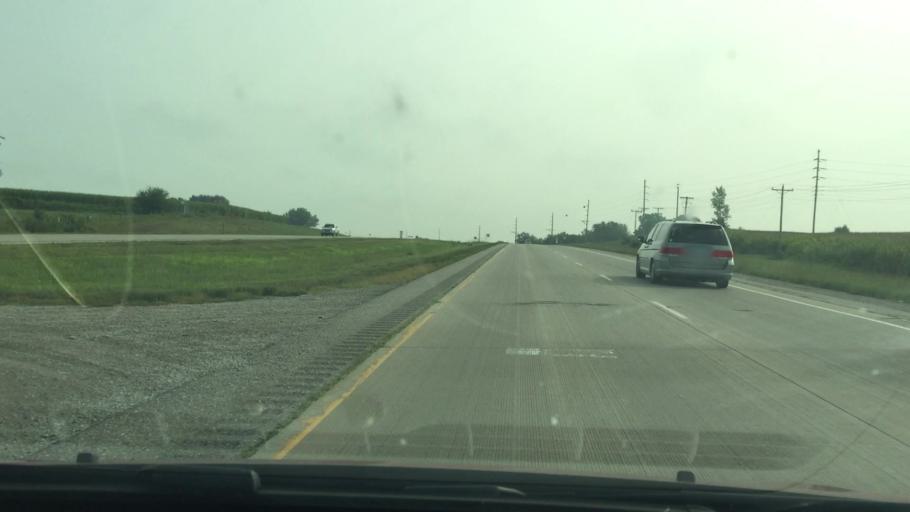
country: US
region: Iowa
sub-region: Muscatine County
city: Muscatine
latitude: 41.4629
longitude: -91.0105
